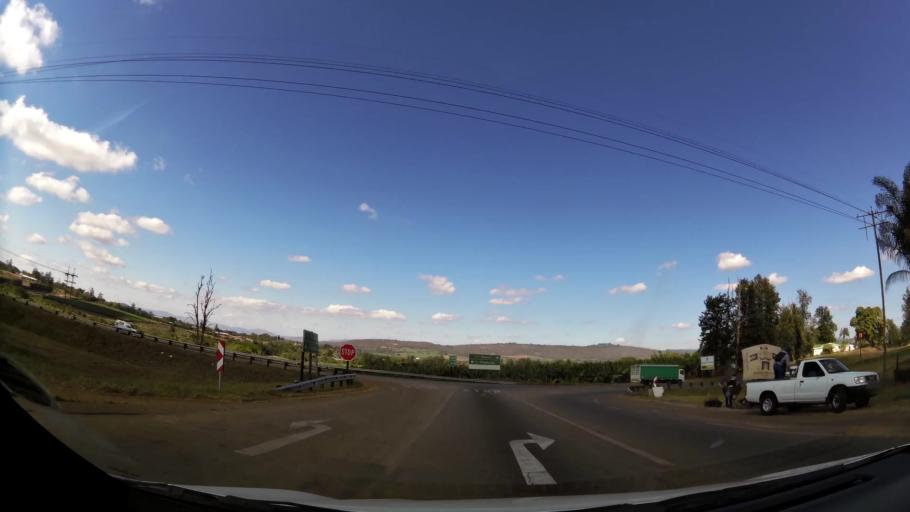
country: ZA
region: Limpopo
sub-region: Mopani District Municipality
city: Tzaneen
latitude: -23.8139
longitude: 30.1731
